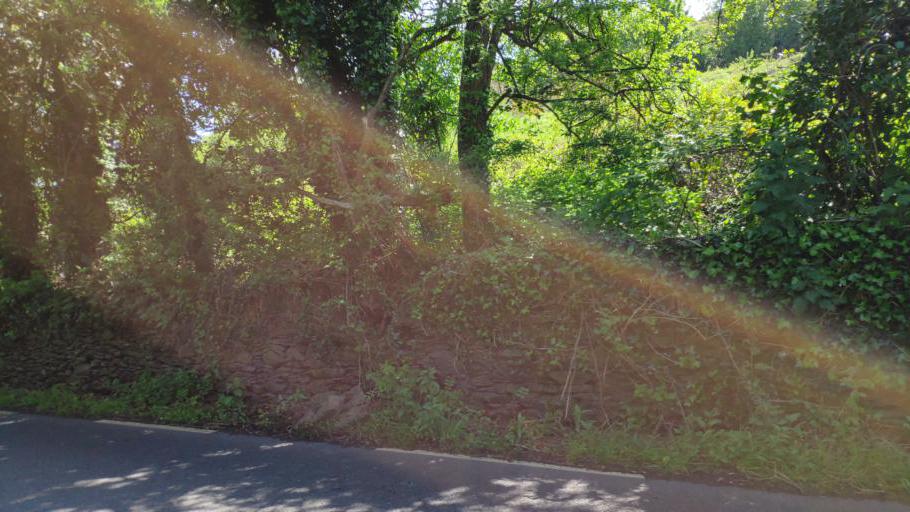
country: IE
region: Munster
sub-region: County Cork
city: Cork
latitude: 51.9219
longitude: -8.4983
